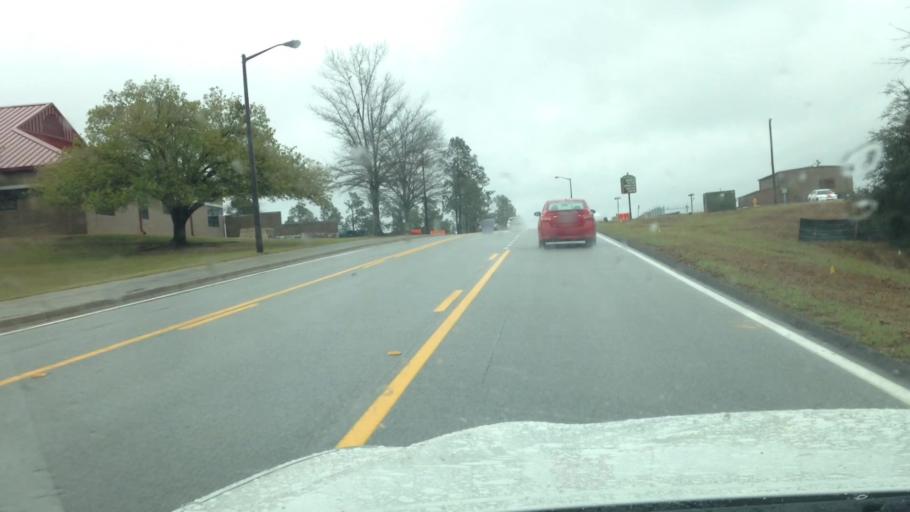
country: US
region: Georgia
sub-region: Columbia County
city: Grovetown
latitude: 33.4160
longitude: -82.1538
